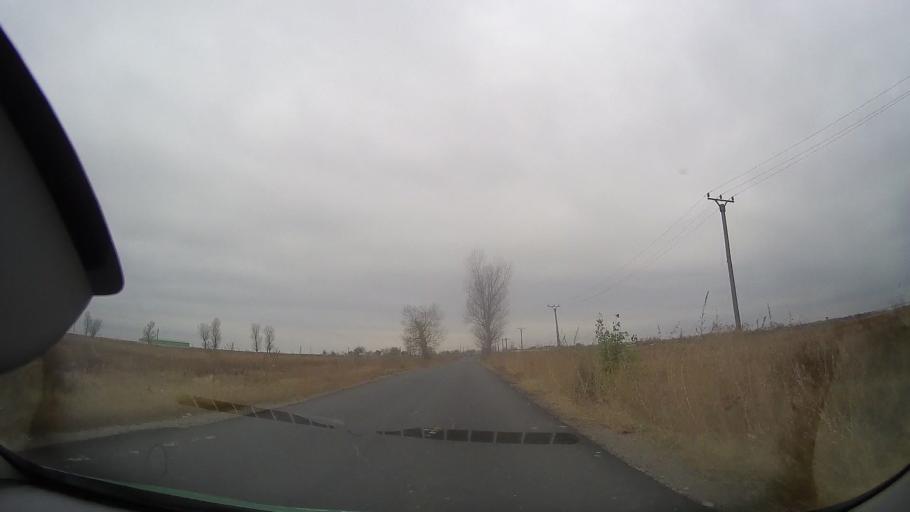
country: RO
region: Braila
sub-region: Comuna Ciresu
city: Ciresu
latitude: 44.9428
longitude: 27.3394
